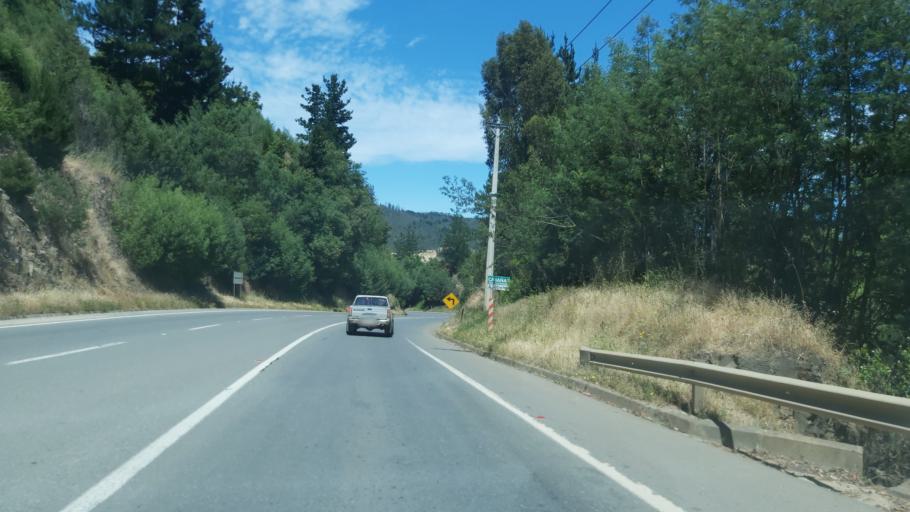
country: CL
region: Maule
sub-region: Provincia de Talca
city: Constitucion
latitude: -35.3328
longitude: -72.3879
